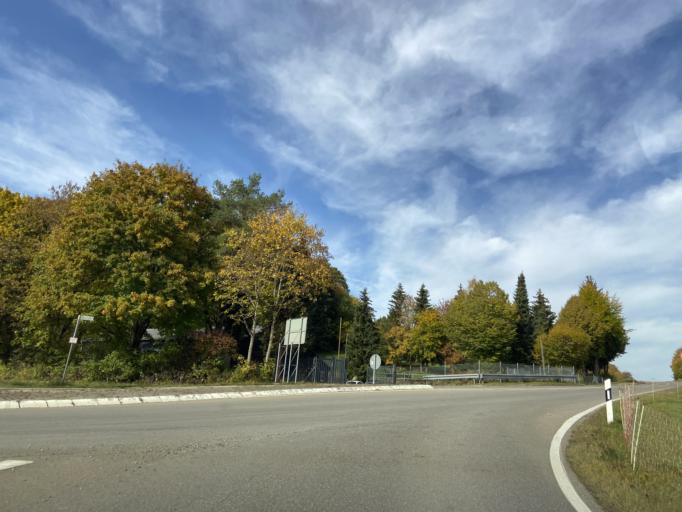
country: DE
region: Baden-Wuerttemberg
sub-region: Tuebingen Region
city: Schwenningen
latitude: 48.1012
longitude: 9.0089
